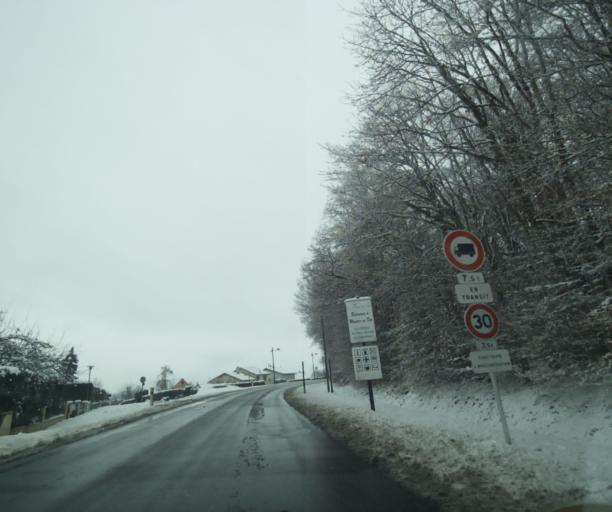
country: FR
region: Champagne-Ardenne
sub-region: Departement de la Haute-Marne
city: Montier-en-Der
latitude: 48.4853
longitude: 4.7744
